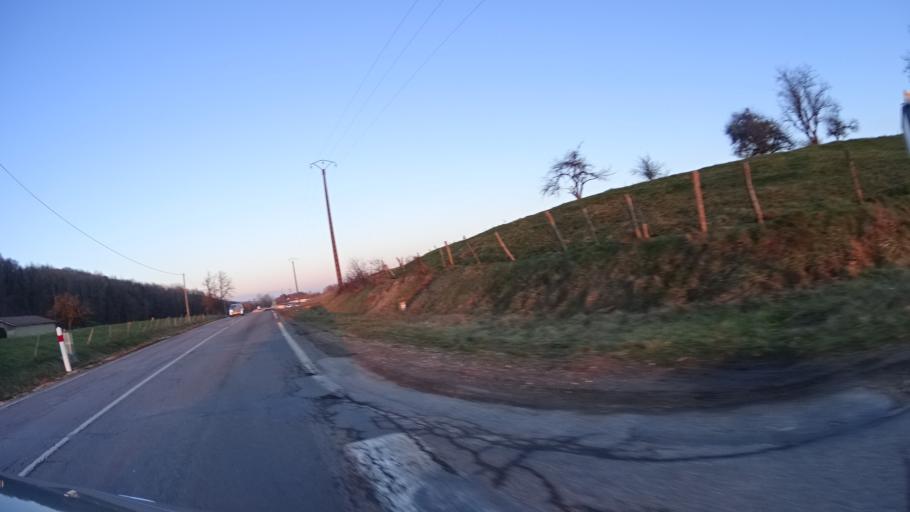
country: FR
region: Franche-Comte
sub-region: Departement du Doubs
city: Morre
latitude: 47.2087
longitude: 6.0538
